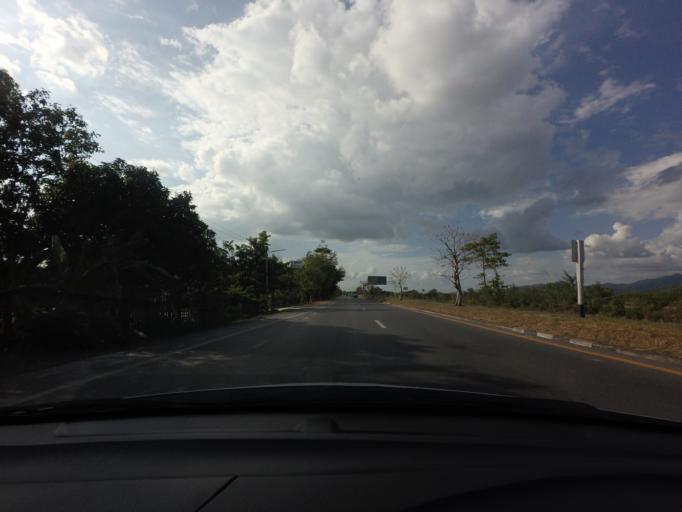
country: TH
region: Nakhon Nayok
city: Nakhon Nayok
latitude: 14.2270
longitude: 101.1918
